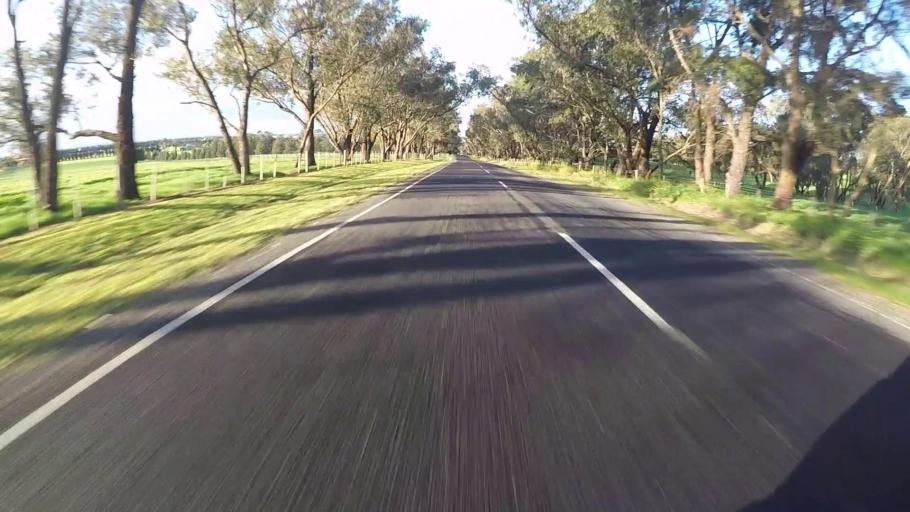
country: AU
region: Victoria
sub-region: Greater Geelong
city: Wandana Heights
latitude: -38.1503
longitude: 144.1773
